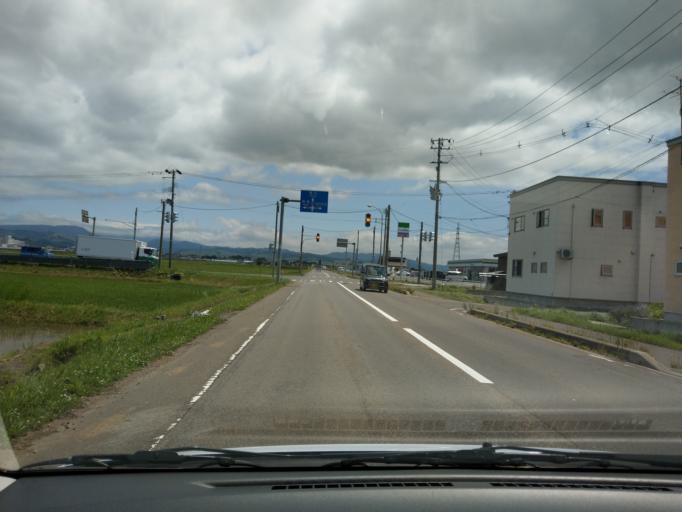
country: JP
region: Aomori
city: Kuroishi
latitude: 40.6592
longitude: 140.5617
